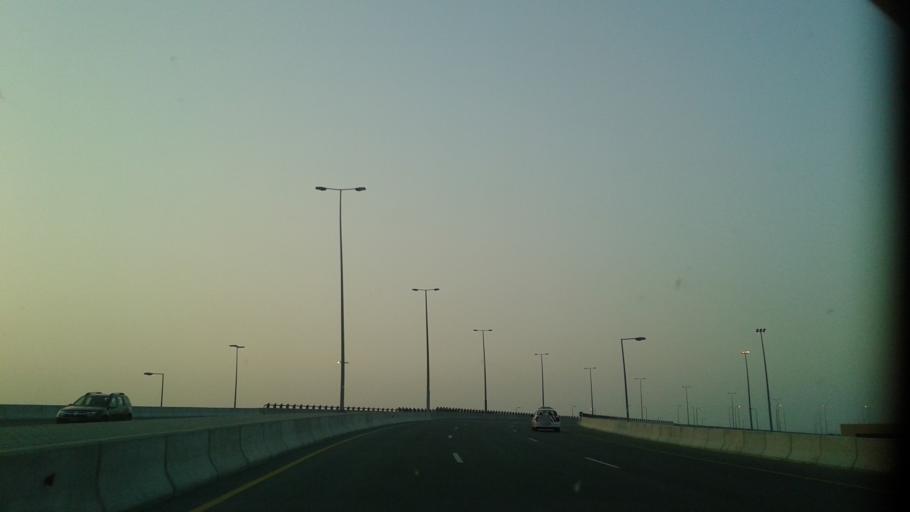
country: OM
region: Muhafazat Masqat
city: Bawshar
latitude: 23.5691
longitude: 58.3347
